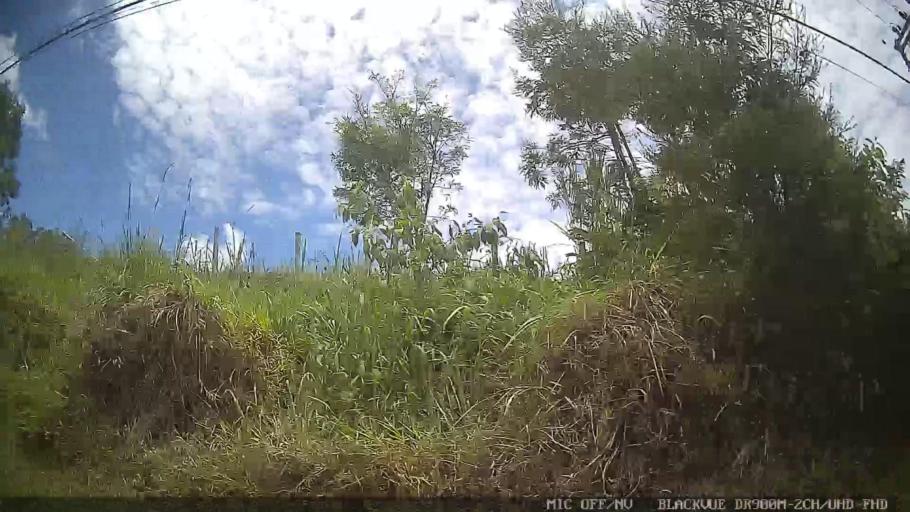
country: BR
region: Sao Paulo
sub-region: Biritiba-Mirim
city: Biritiba Mirim
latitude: -23.5398
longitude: -45.9161
